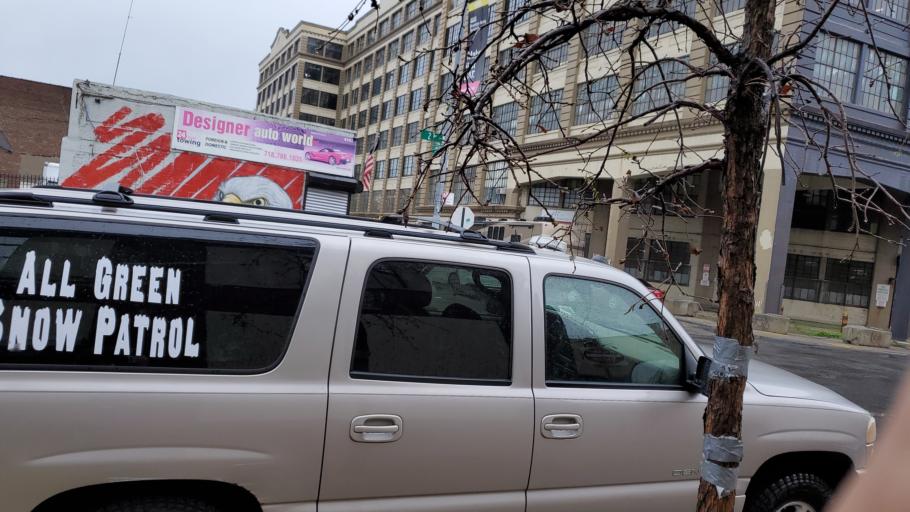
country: US
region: New York
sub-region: Kings County
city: Bensonhurst
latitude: 40.6540
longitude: -74.0118
